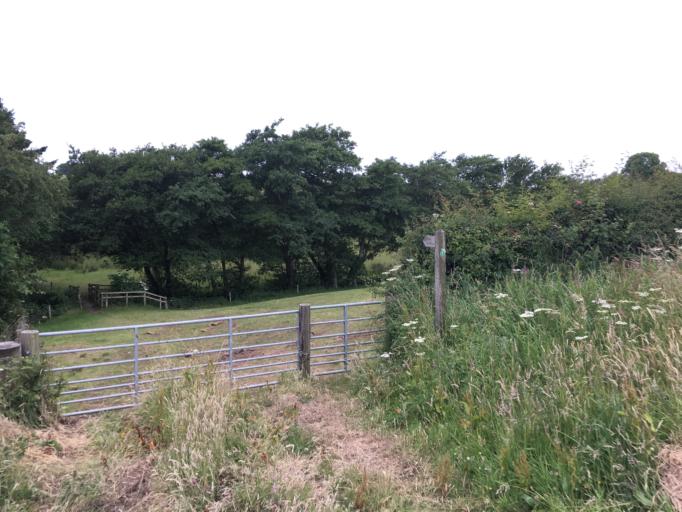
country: GB
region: England
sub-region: Northumberland
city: Lowick
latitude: 55.6612
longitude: -1.9091
